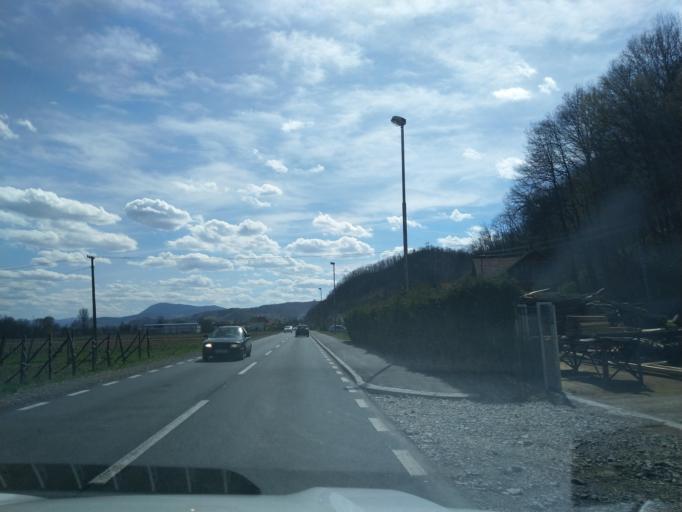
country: RS
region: Central Serbia
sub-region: Zlatiborski Okrug
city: Arilje
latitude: 43.7777
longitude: 20.1025
